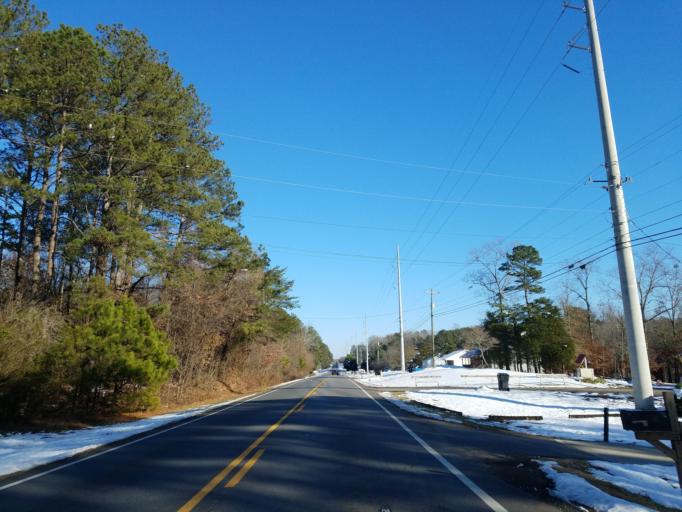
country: US
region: Georgia
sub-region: Dawson County
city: Dawsonville
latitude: 34.3537
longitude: -84.0771
